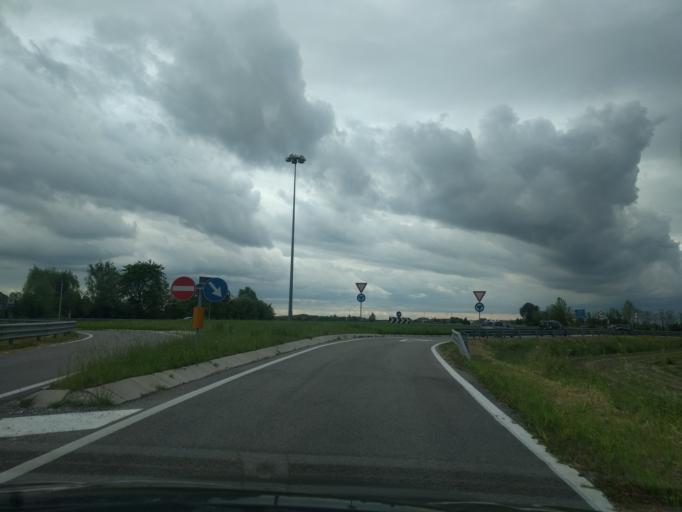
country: IT
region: Veneto
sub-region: Provincia di Rovigo
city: Buso
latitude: 45.0767
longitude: 11.8549
